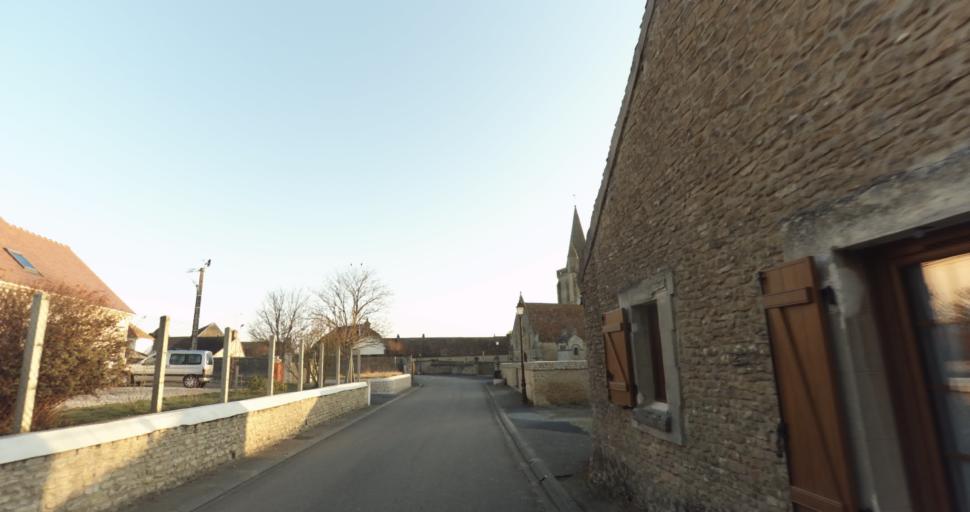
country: FR
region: Lower Normandy
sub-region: Departement du Calvados
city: Saint-Pierre-sur-Dives
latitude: 49.0358
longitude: -0.0269
